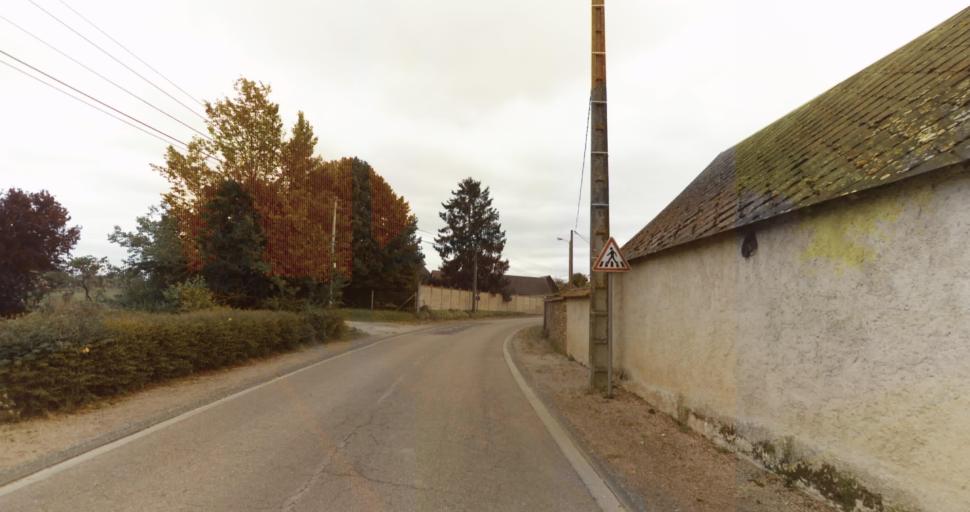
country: FR
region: Haute-Normandie
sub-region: Departement de l'Eure
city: Pacy-sur-Eure
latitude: 48.9508
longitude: 1.3039
